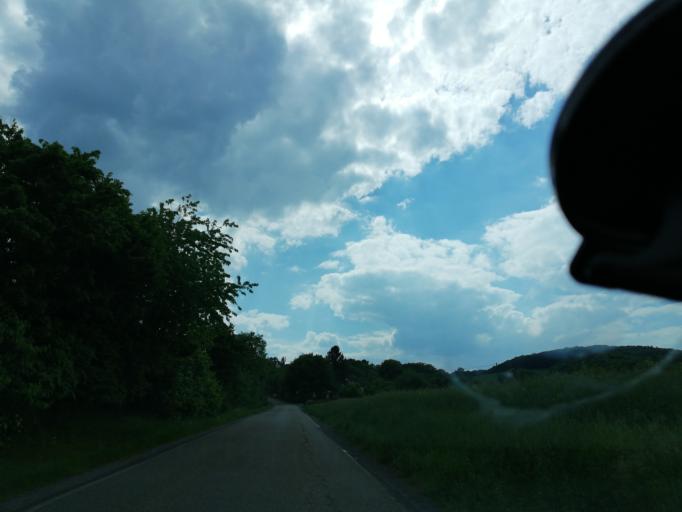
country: DE
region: North Rhine-Westphalia
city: Wetter (Ruhr)
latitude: 51.3874
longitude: 7.3607
